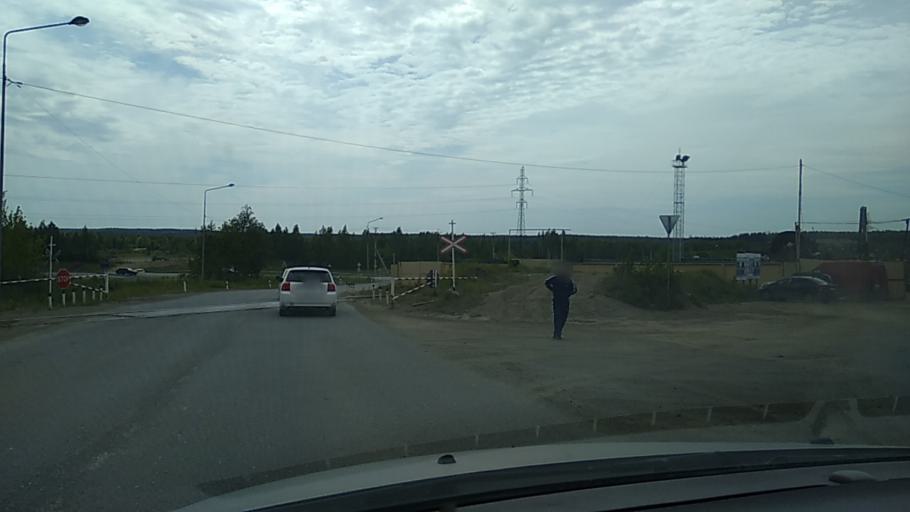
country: RU
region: Sverdlovsk
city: Verkhnyaya Pyshma
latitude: 56.9537
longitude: 60.5862
